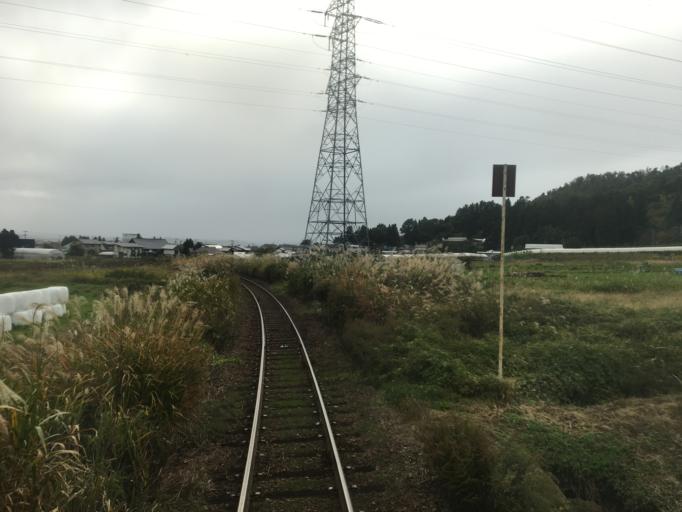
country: JP
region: Yamagata
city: Nagai
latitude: 38.0564
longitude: 140.0939
